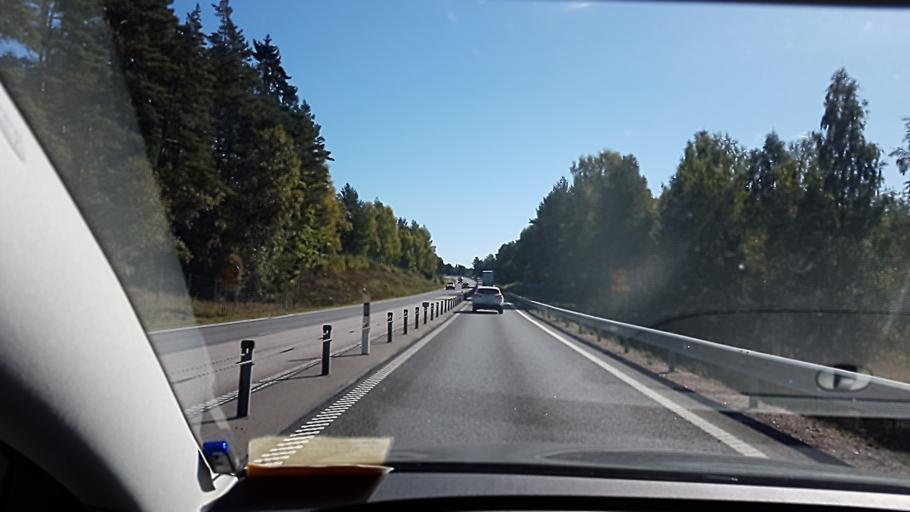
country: SE
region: Kronoberg
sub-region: Vaxjo Kommun
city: Ingelstad
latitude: 56.8705
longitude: 14.9635
